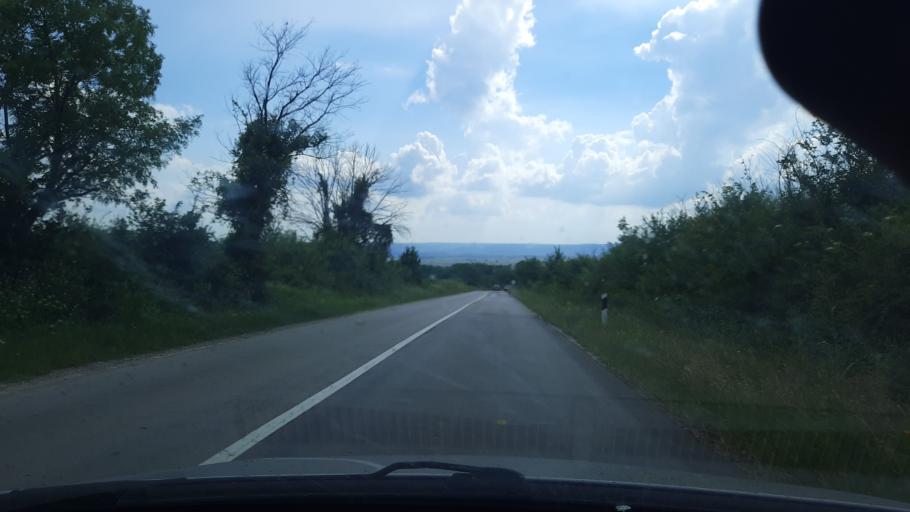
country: RS
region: Central Serbia
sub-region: Branicevski Okrug
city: Malo Crnice
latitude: 44.5775
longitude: 21.3835
